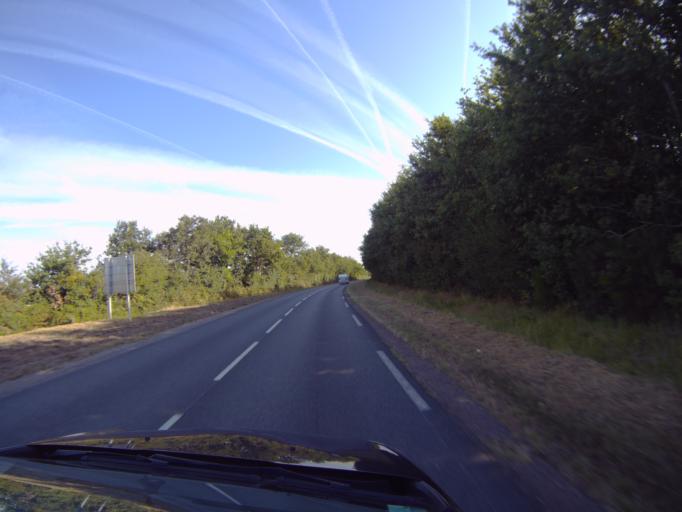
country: FR
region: Pays de la Loire
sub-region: Departement de la Vendee
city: Saint-Hilaire-de-Talmont
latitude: 46.4932
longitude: -1.5842
